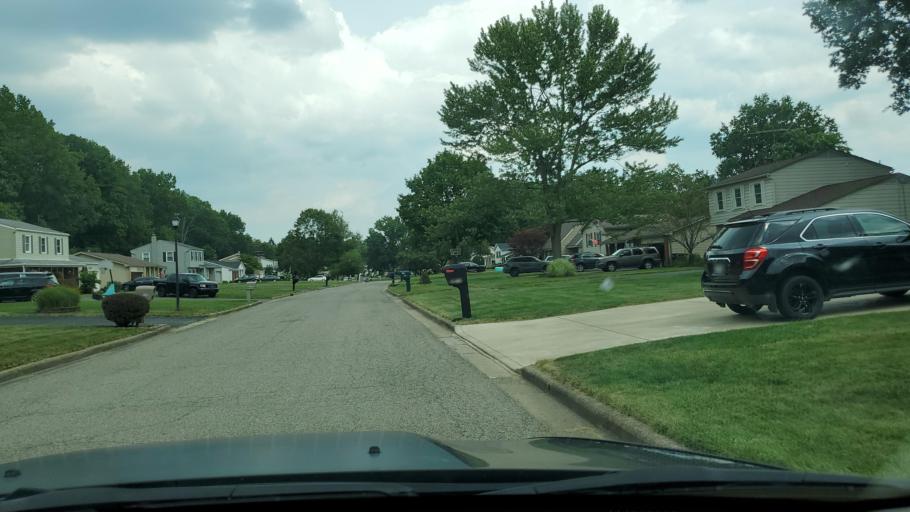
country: US
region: Ohio
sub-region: Trumbull County
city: Bolindale
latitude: 41.2284
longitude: -80.7704
